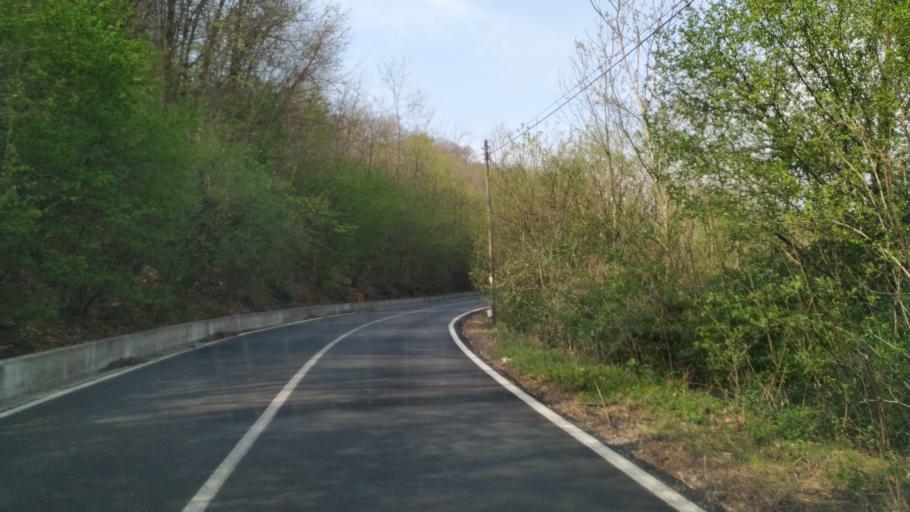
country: IT
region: Piedmont
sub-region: Provincia di Novara
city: Pogno
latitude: 45.7565
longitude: 8.3951
